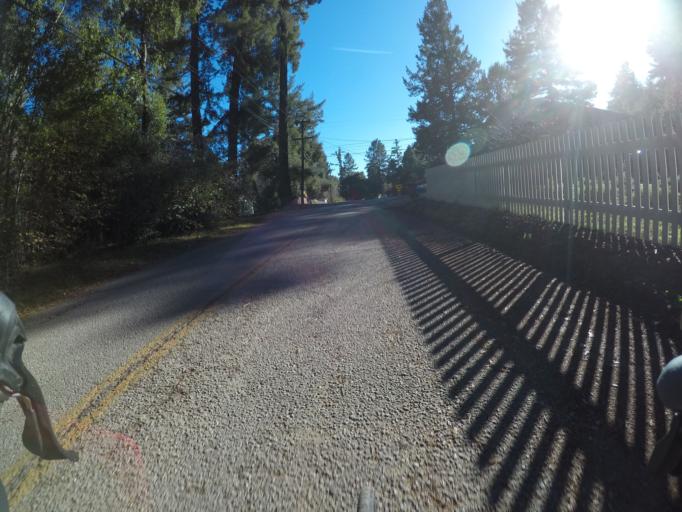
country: US
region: California
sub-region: Santa Cruz County
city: Felton
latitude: 37.0393
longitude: -122.0765
